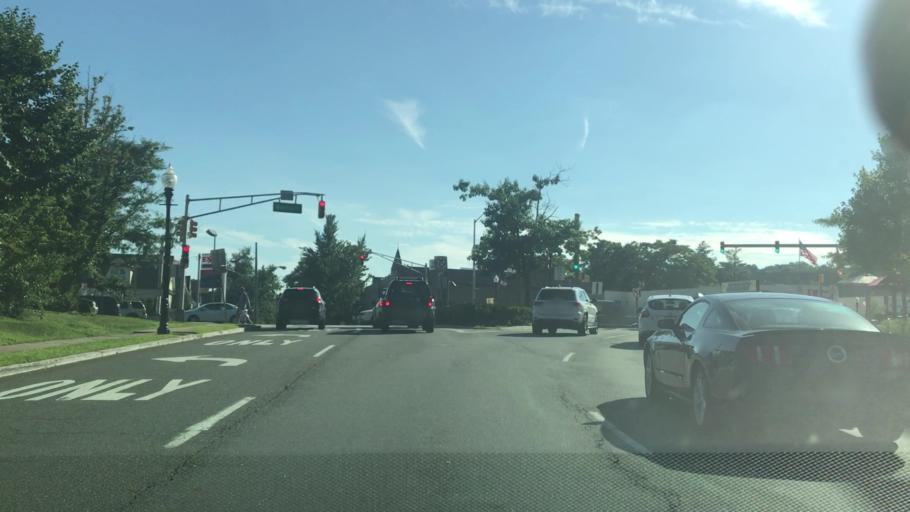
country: US
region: New Jersey
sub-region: Morris County
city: Morristown
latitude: 40.7974
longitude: -74.4755
